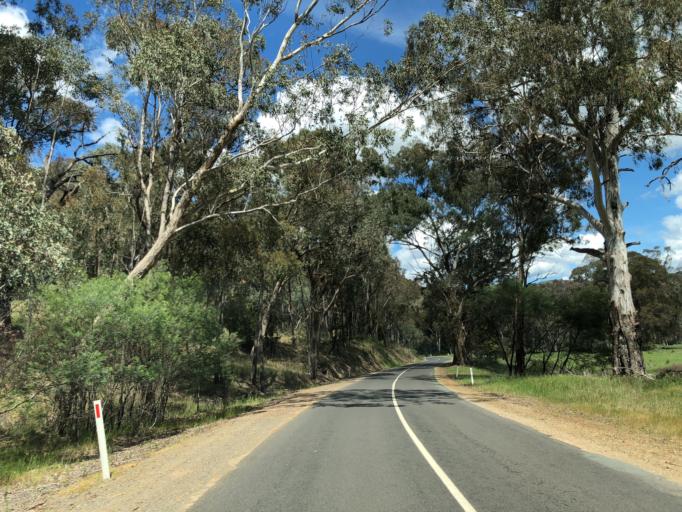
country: AU
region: Victoria
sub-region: Benalla
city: Benalla
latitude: -36.7541
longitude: 146.1196
